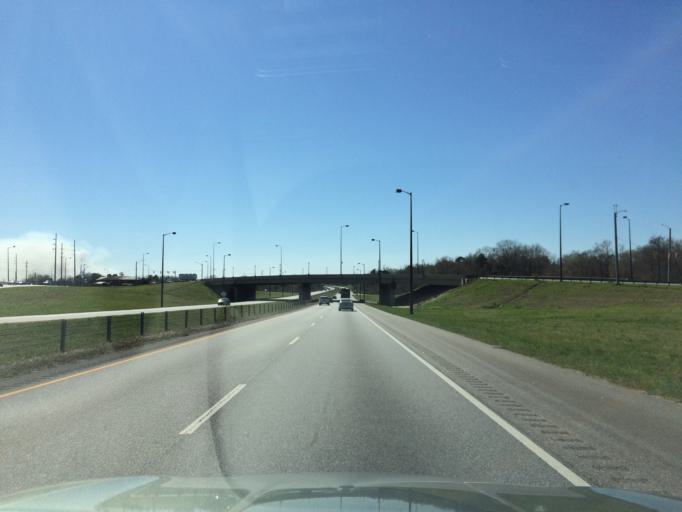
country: US
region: Alabama
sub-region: Lee County
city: Auburn
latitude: 32.5600
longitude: -85.5037
